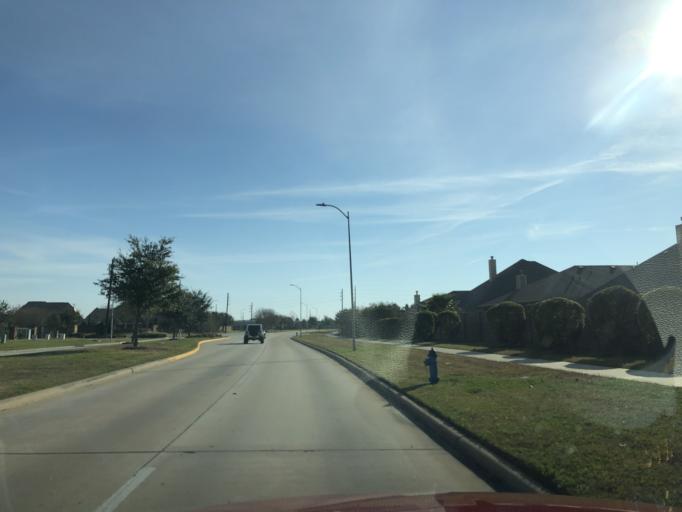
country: US
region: Texas
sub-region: Harris County
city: Tomball
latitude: 30.0551
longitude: -95.5735
